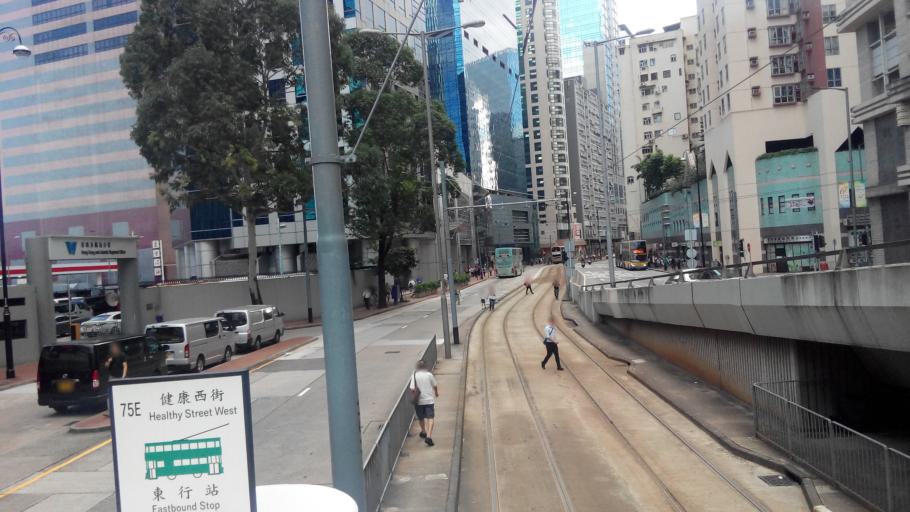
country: HK
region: Kowloon City
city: Kowloon
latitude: 22.2921
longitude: 114.2052
